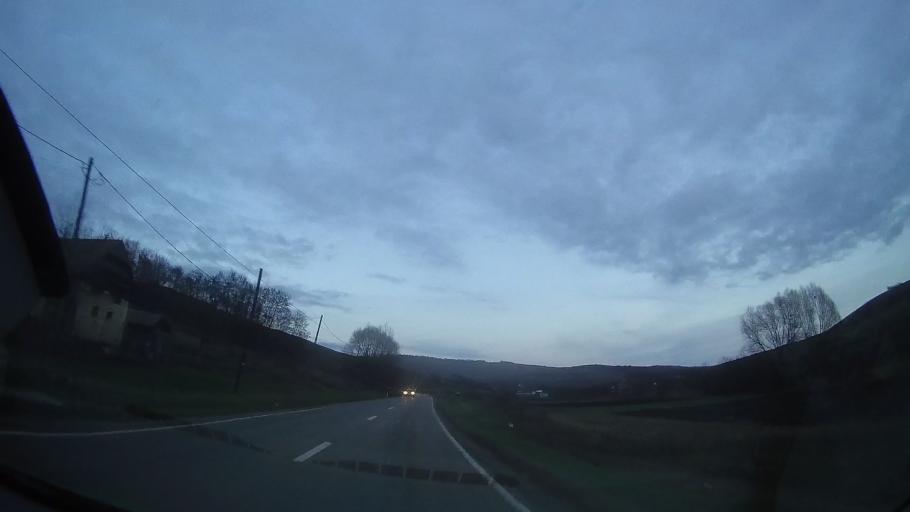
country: RO
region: Cluj
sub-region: Comuna Caianu
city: Vaida-Camaras
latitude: 46.8019
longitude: 23.9567
